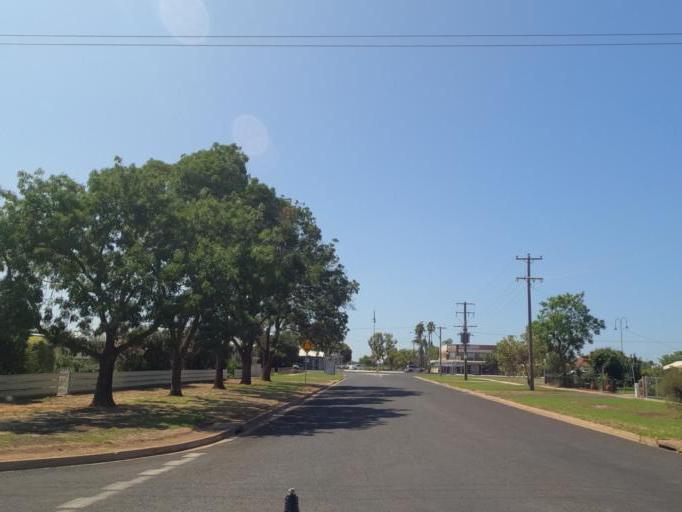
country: AU
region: New South Wales
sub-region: Corowa Shire
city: Mulwala
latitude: -35.9887
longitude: 146.0041
